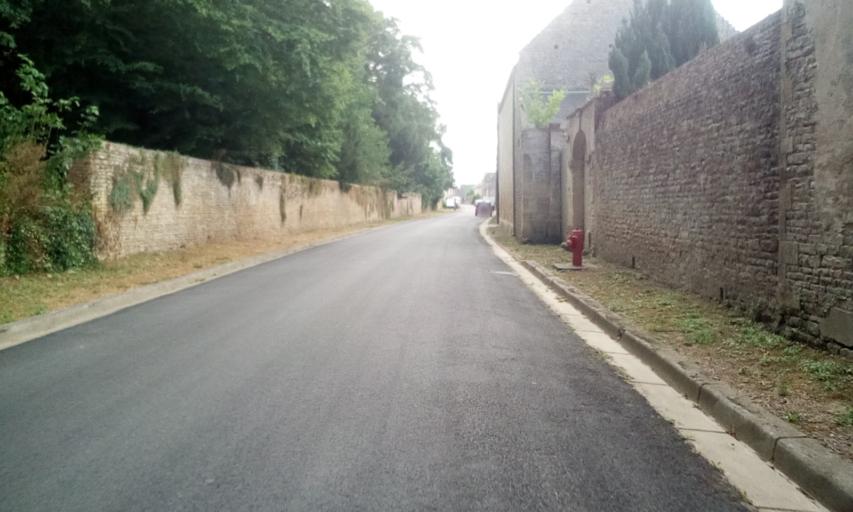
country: FR
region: Lower Normandy
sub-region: Departement du Calvados
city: Courseulles-sur-Mer
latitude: 49.3107
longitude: -0.4907
